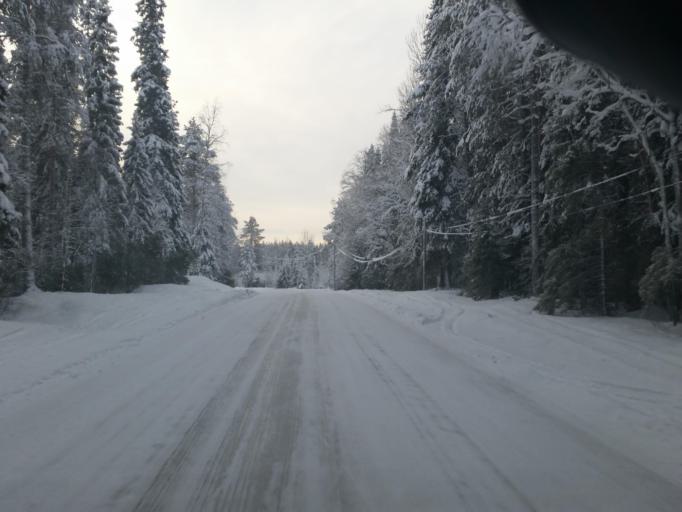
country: SE
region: Norrbotten
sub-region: Pitea Kommun
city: Norrfjarden
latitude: 65.5670
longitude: 21.4821
